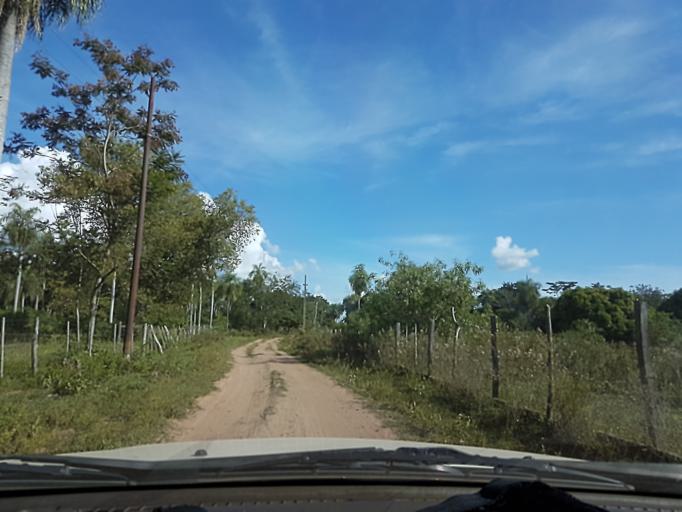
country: PY
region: Cordillera
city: Arroyos y Esteros
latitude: -24.9752
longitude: -57.1942
